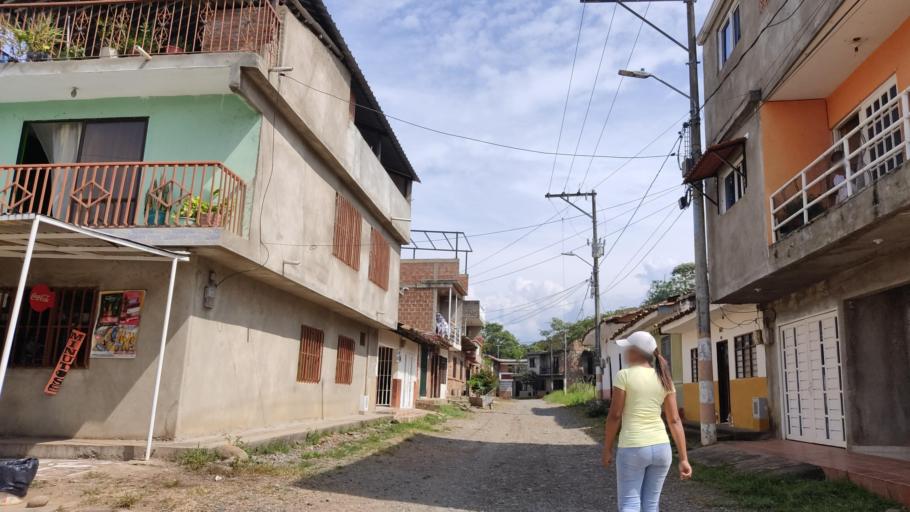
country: CO
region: Cauca
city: Buenos Aires
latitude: 3.1289
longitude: -76.5921
